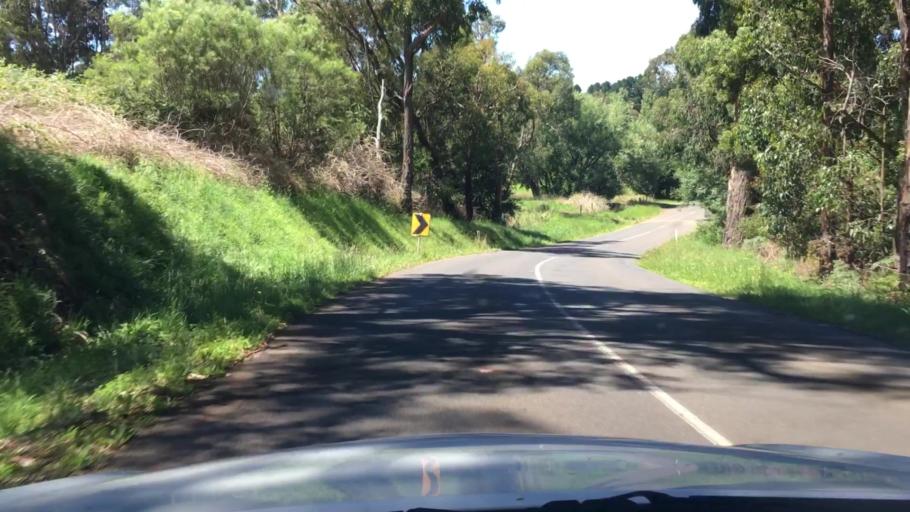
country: AU
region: Victoria
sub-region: Yarra Ranges
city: Mount Evelyn
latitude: -37.8058
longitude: 145.4090
